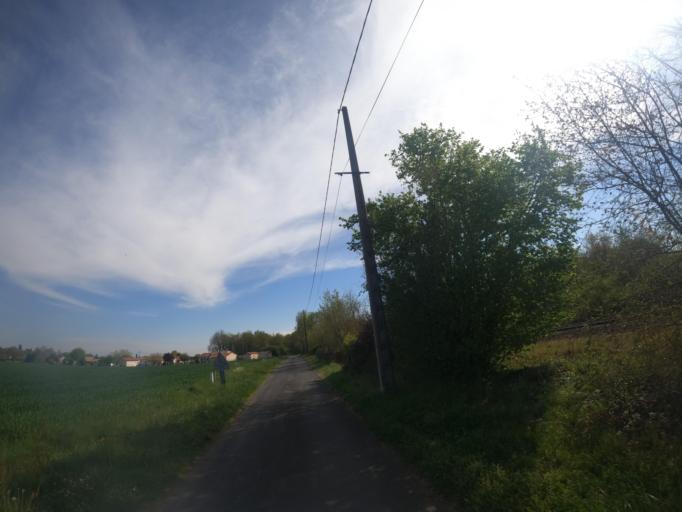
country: FR
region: Poitou-Charentes
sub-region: Departement des Deux-Sevres
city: Saint-Jean-de-Thouars
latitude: 46.9288
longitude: -0.2266
